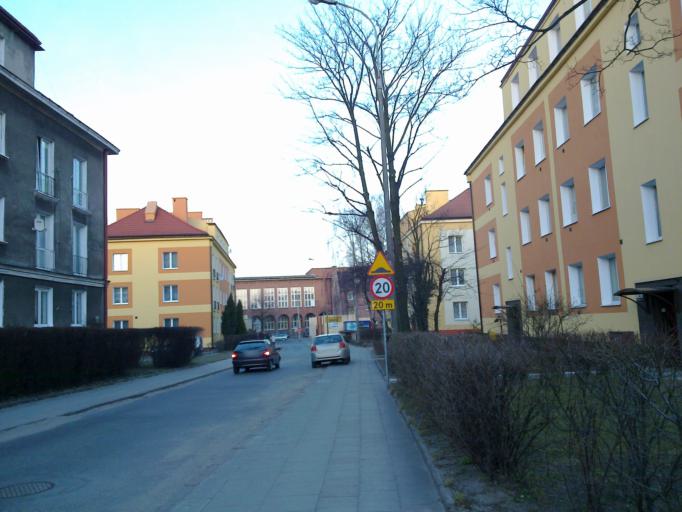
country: PL
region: Pomeranian Voivodeship
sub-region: Gdansk
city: Gdansk
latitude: 54.3853
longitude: 18.6072
